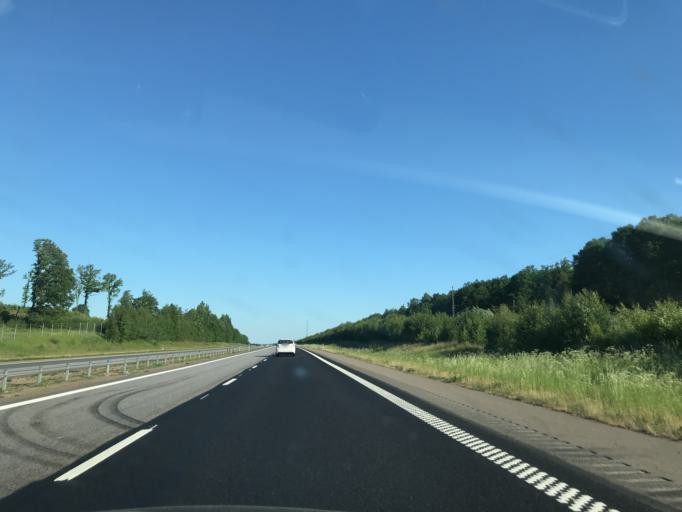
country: SE
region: Halland
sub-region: Halmstads Kommun
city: Aled
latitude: 56.7439
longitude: 12.8656
